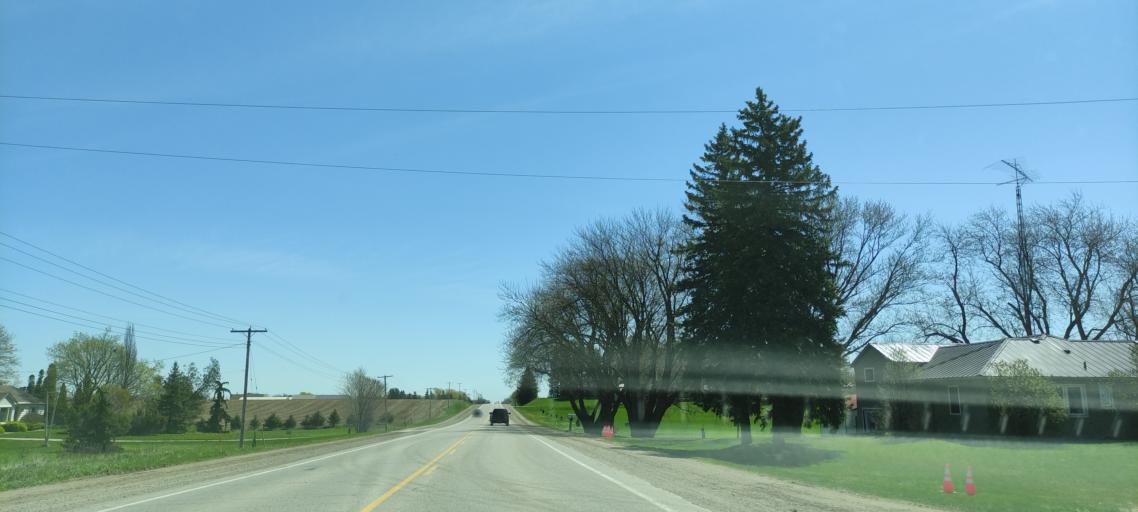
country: CA
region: Ontario
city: Waterloo
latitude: 43.6035
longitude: -80.5970
